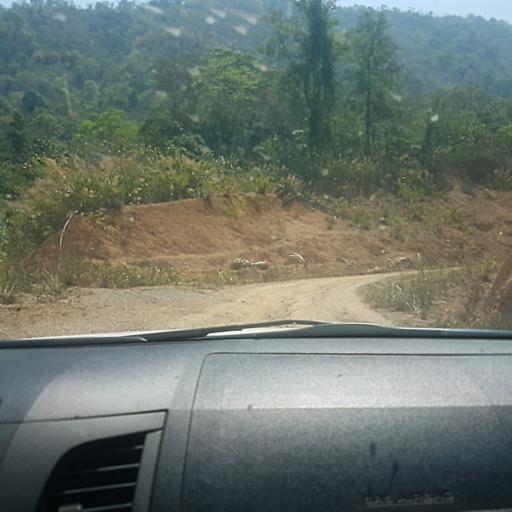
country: LA
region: Bolikhamxai
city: Ban Nahin
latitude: 18.5449
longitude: 104.5675
